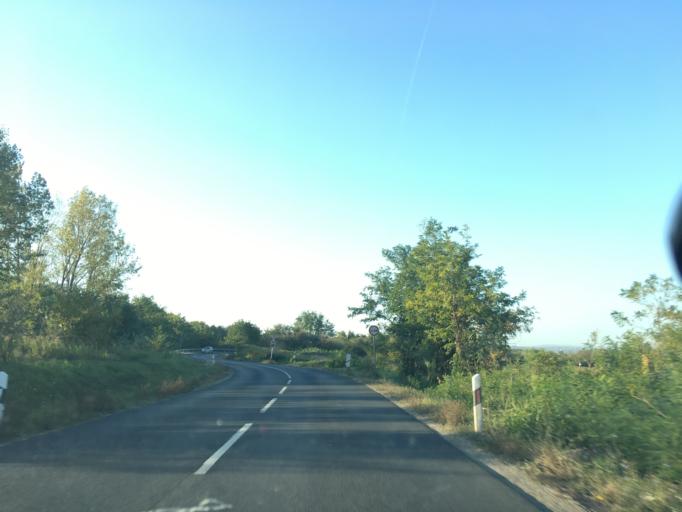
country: HU
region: Pest
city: Szazhalombatta
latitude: 47.3299
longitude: 18.8953
